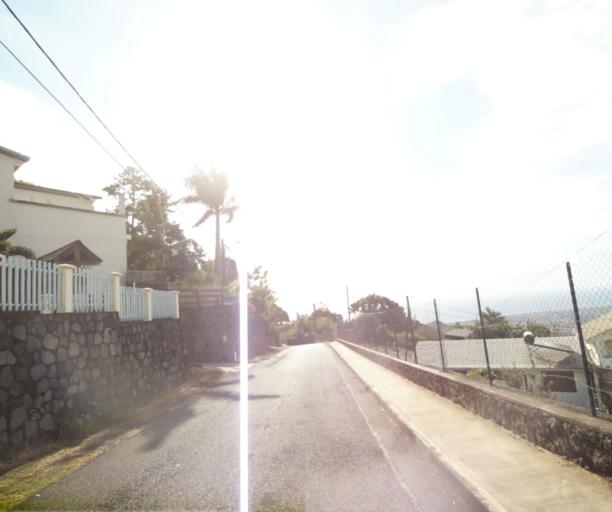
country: RE
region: Reunion
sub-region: Reunion
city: Saint-Paul
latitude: -20.9972
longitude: 55.3321
